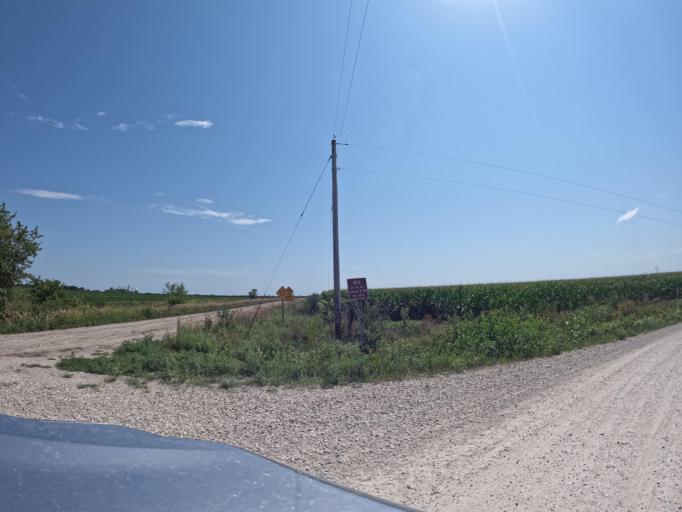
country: US
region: Iowa
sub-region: Henry County
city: Mount Pleasant
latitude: 40.8902
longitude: -91.6318
